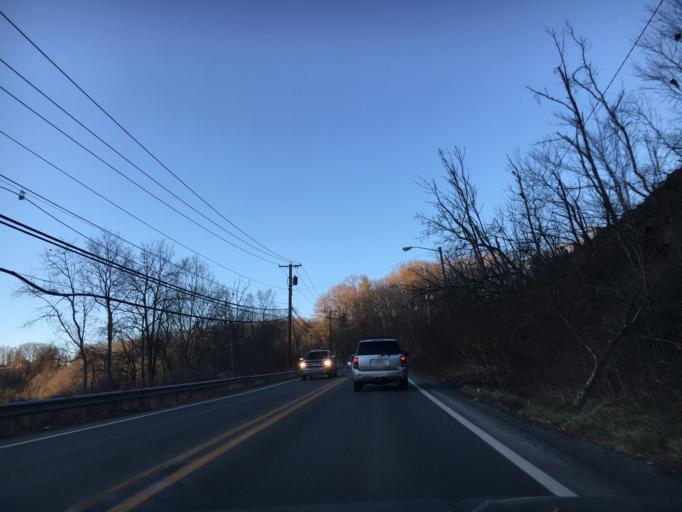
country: US
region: West Virginia
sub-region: Raleigh County
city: Beaver
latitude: 37.7584
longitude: -81.1577
